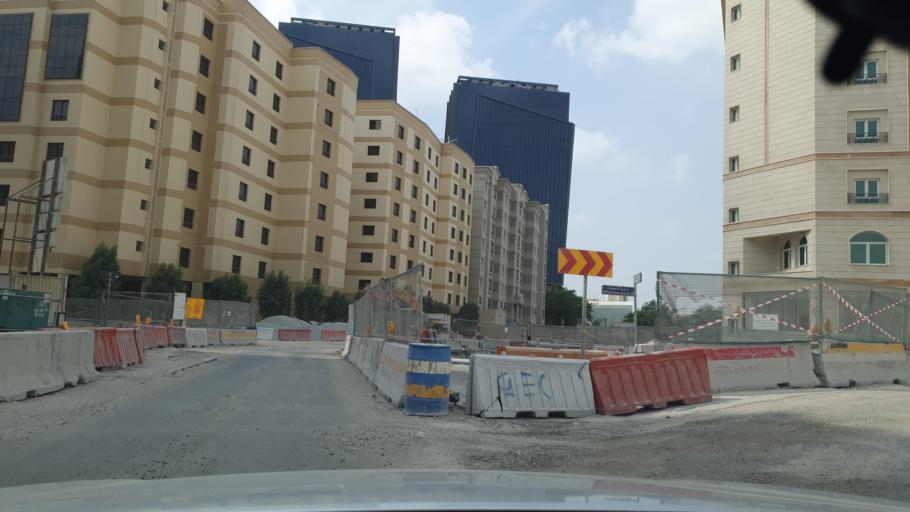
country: QA
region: Baladiyat ad Dawhah
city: Doha
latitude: 25.2818
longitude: 51.5101
